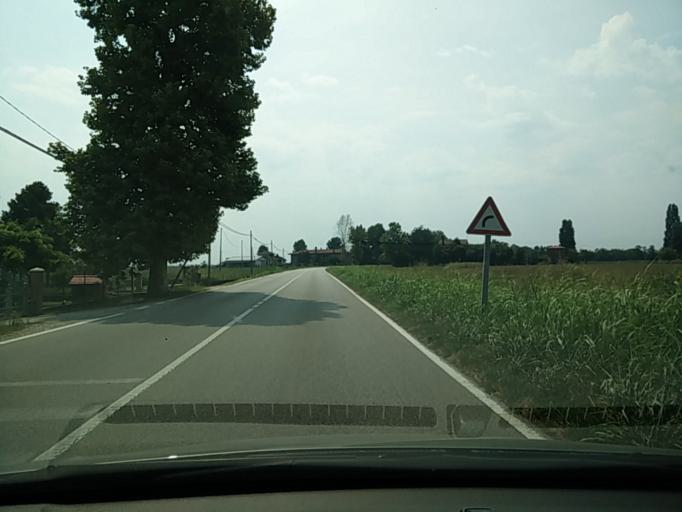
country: IT
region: Veneto
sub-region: Provincia di Venezia
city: Torre di Mosto
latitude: 45.6544
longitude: 12.6904
